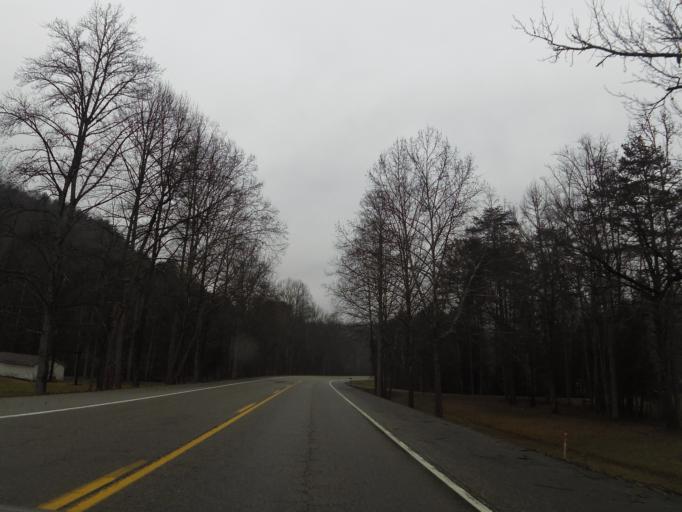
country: US
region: Tennessee
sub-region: Roane County
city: Harriman
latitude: 36.0027
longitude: -84.5113
